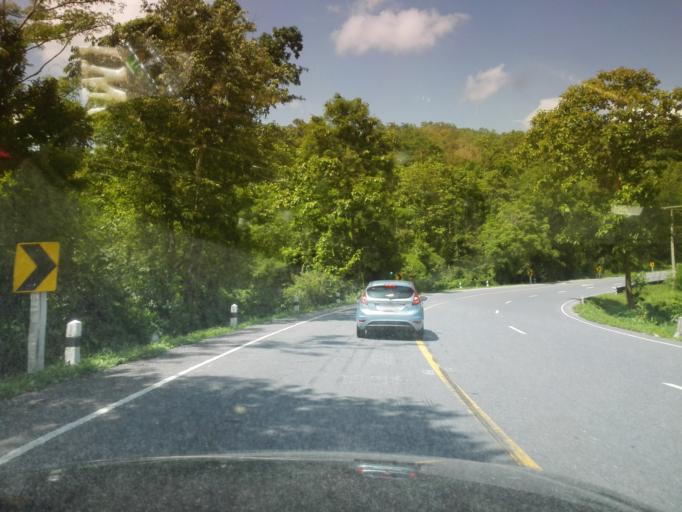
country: TH
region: Tak
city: Mae Sot
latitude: 16.7562
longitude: 98.7258
